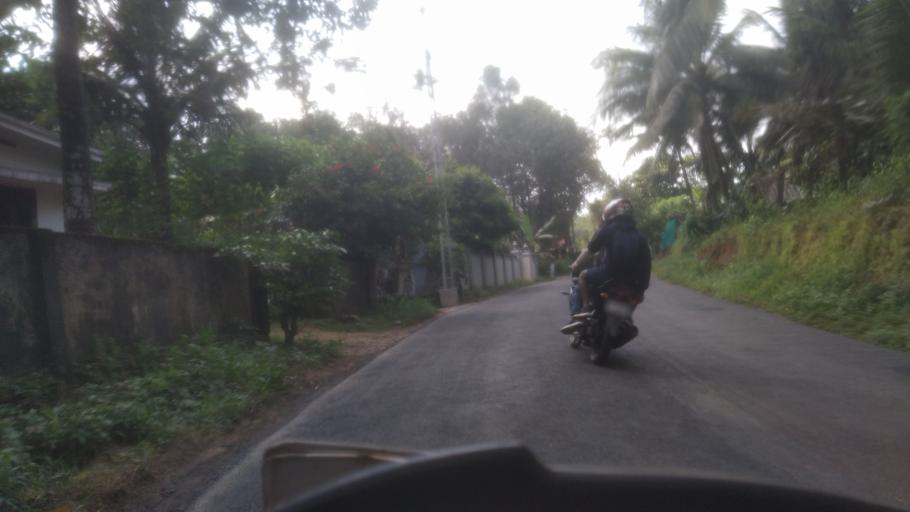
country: IN
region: Kerala
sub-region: Ernakulam
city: Kotamangalam
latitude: 10.0019
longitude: 76.7330
